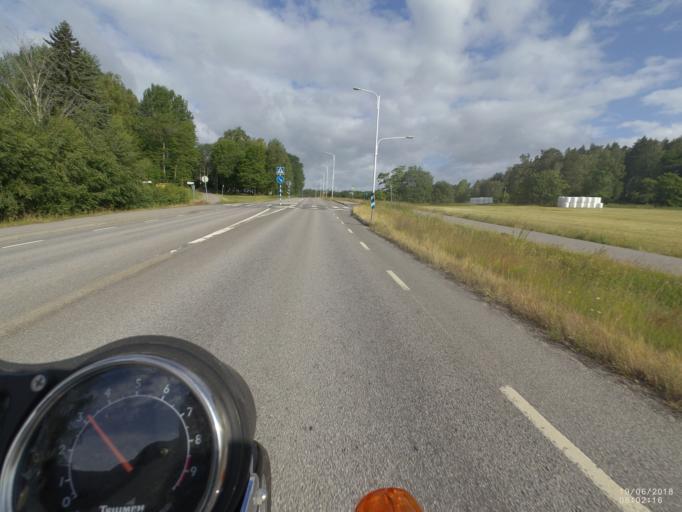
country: SE
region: Soedermanland
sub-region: Nykopings Kommun
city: Nykoping
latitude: 58.7787
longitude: 16.9916
